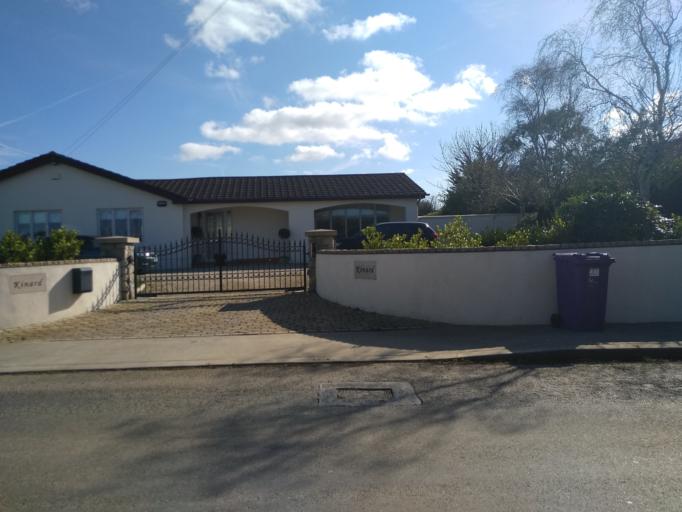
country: IE
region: Leinster
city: Malahide
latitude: 53.4357
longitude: -6.1668
